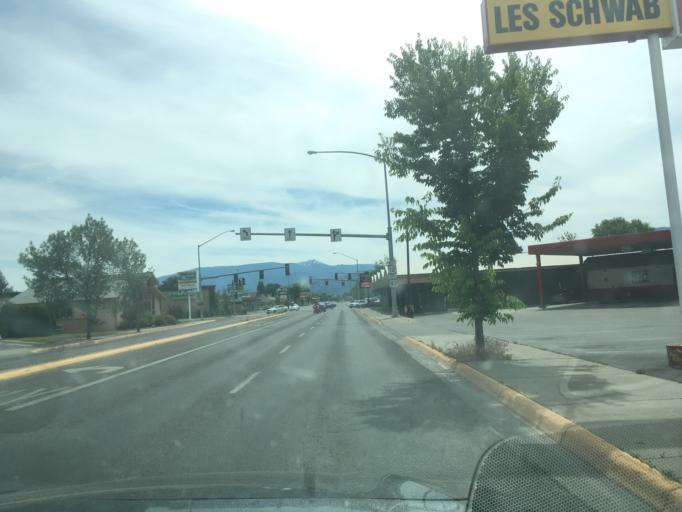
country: US
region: Montana
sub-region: Missoula County
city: Orchard Homes
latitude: 46.8469
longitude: -114.0210
